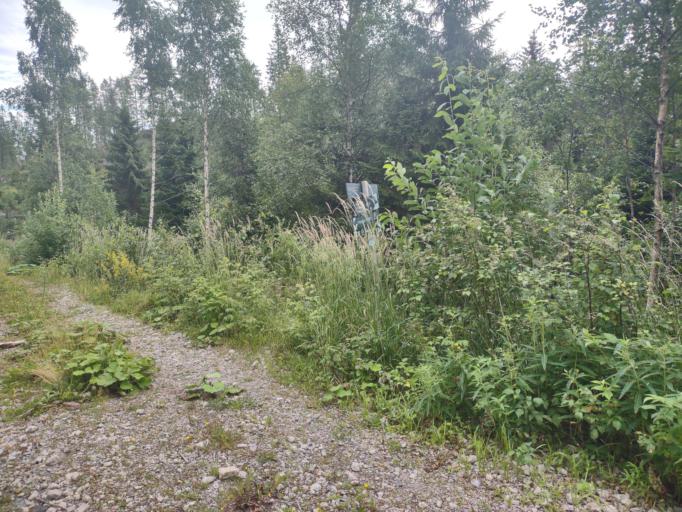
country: NO
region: Akershus
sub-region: Enebakk
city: Flateby
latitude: 59.8151
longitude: 11.0841
